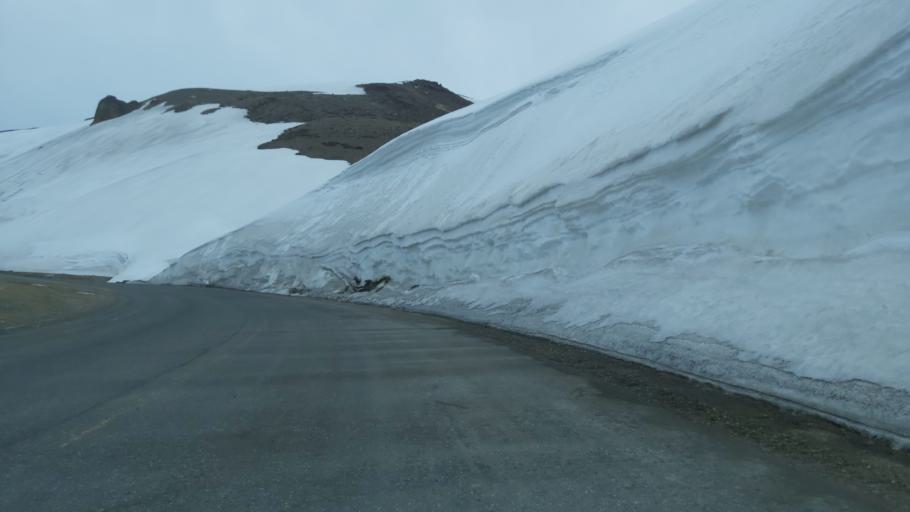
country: CL
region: Maule
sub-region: Provincia de Linares
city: Colbun
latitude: -36.0143
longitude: -70.4956
